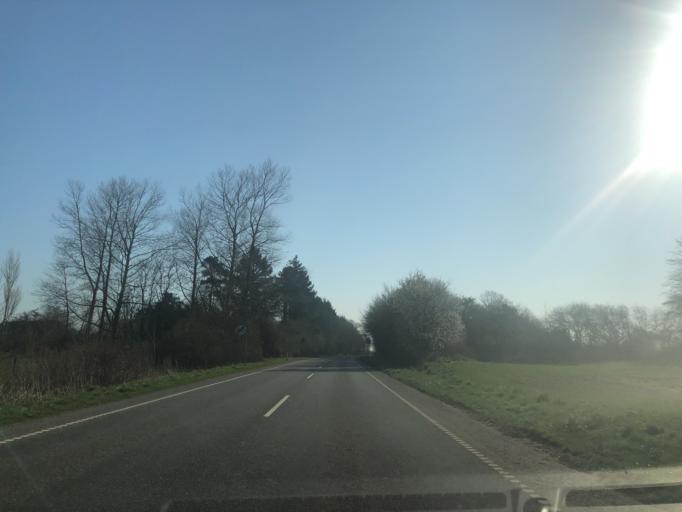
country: DK
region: Zealand
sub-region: Faxe Kommune
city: Fakse
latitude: 55.2688
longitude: 12.1117
